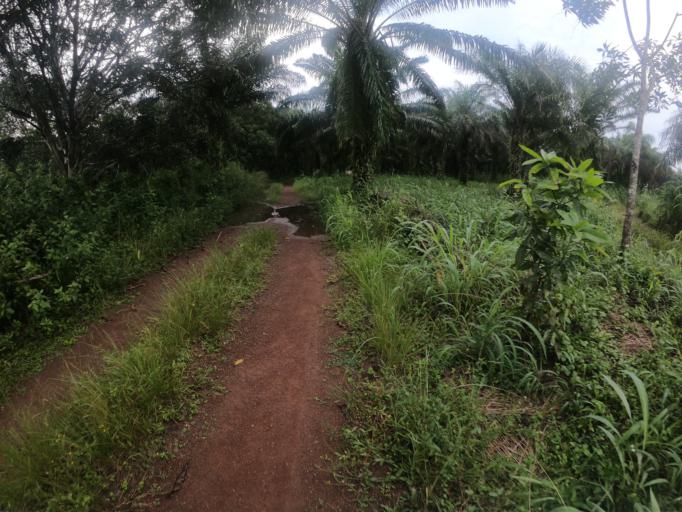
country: SL
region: Southern Province
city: Rotifunk
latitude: 8.4850
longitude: -12.7403
